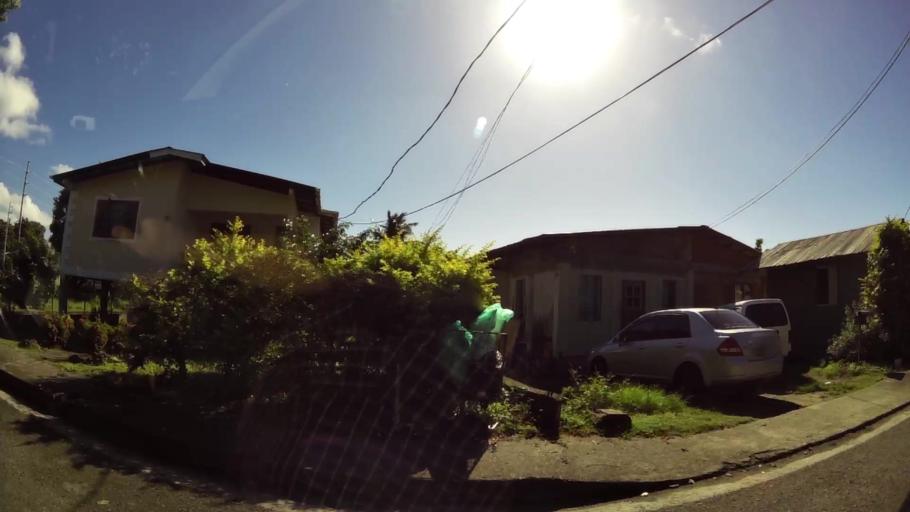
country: TT
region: Tobago
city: Scarborough
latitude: 11.1617
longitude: -60.8103
